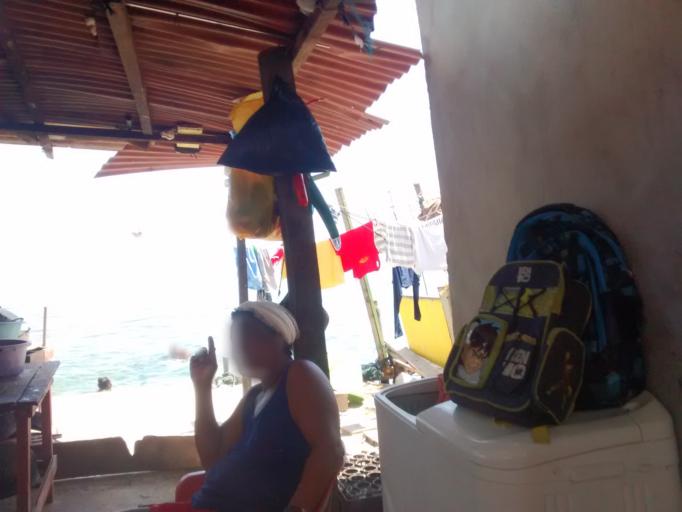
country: CO
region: Sucre
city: San Onofre
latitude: 9.7857
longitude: -75.8596
